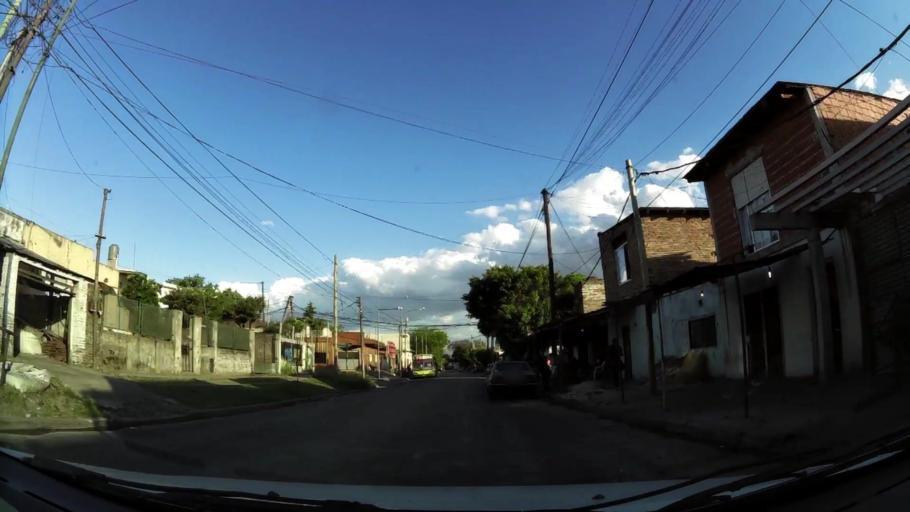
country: AR
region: Buenos Aires
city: Caseros
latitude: -34.5601
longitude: -58.5676
